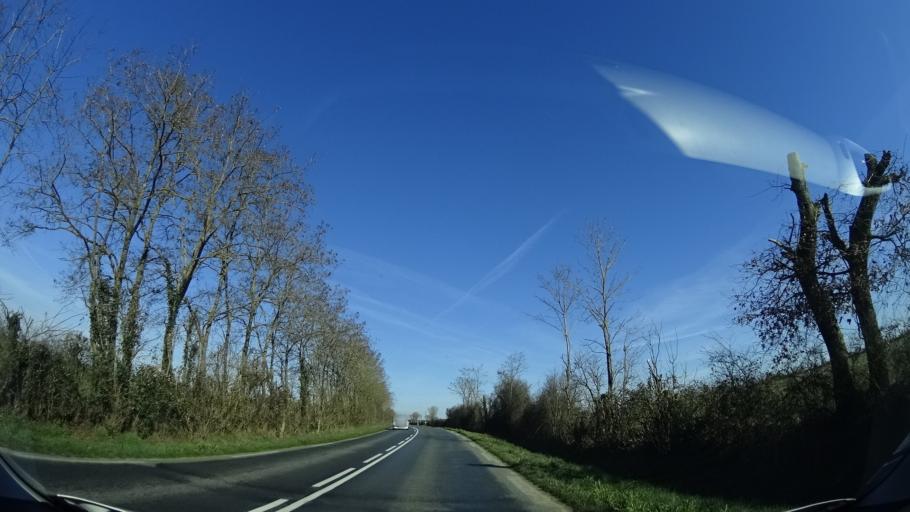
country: FR
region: Poitou-Charentes
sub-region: Departement des Deux-Sevres
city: Saint-Pierre-des-Echaubrognes
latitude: 46.9450
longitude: -0.7533
